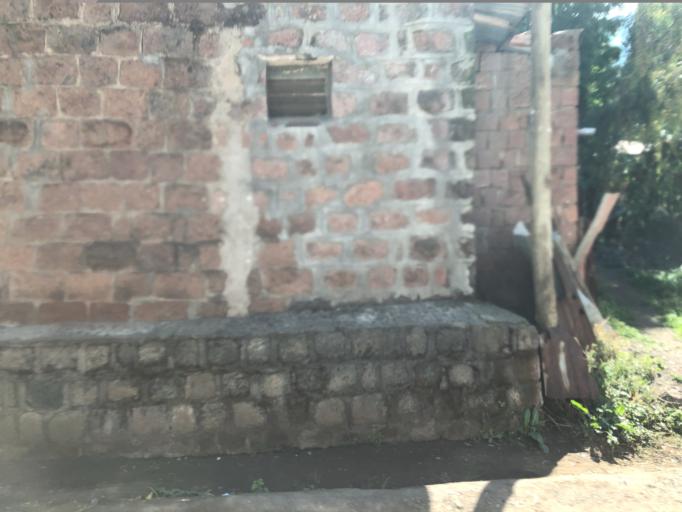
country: ET
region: Amhara
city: Lalibela
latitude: 12.0345
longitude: 39.0491
